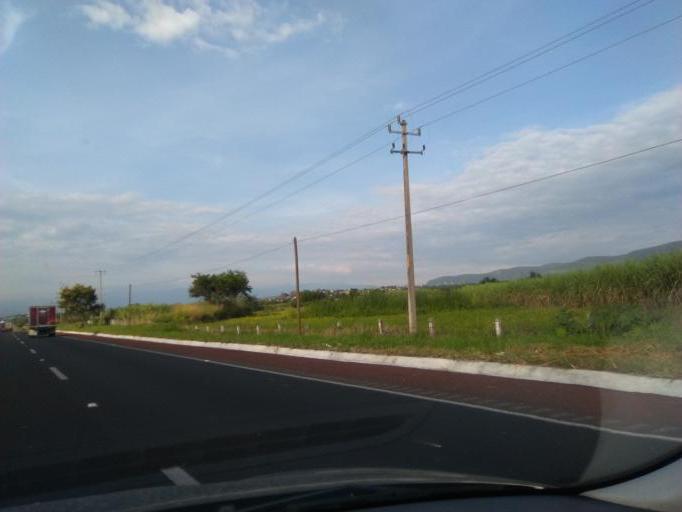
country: MX
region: Morelos
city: Xochitepec
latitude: 18.7865
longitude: -99.2218
